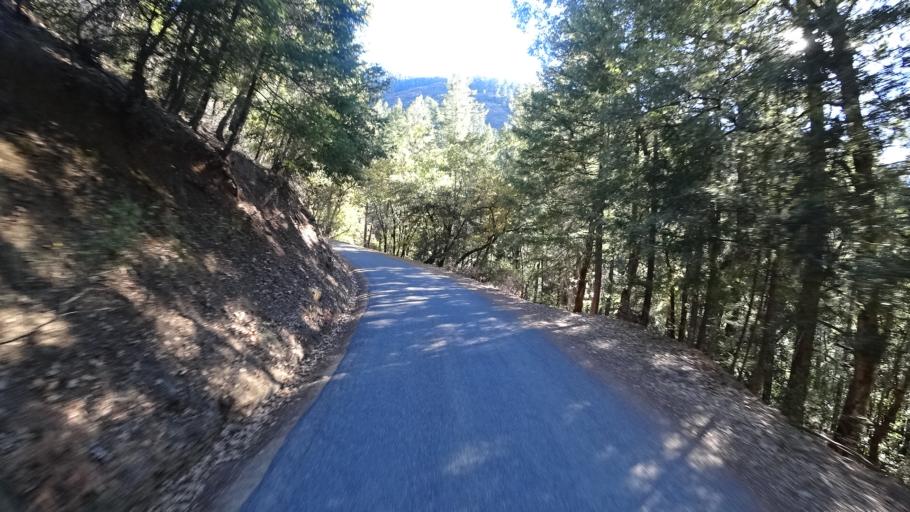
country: US
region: California
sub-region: Siskiyou County
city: Happy Camp
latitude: 41.2992
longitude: -123.2214
